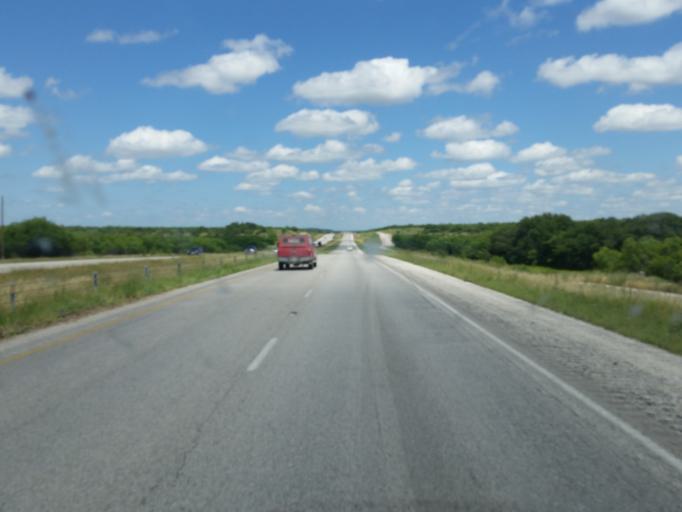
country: US
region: Texas
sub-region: Callahan County
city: Baird
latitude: 32.3823
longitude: -99.2776
